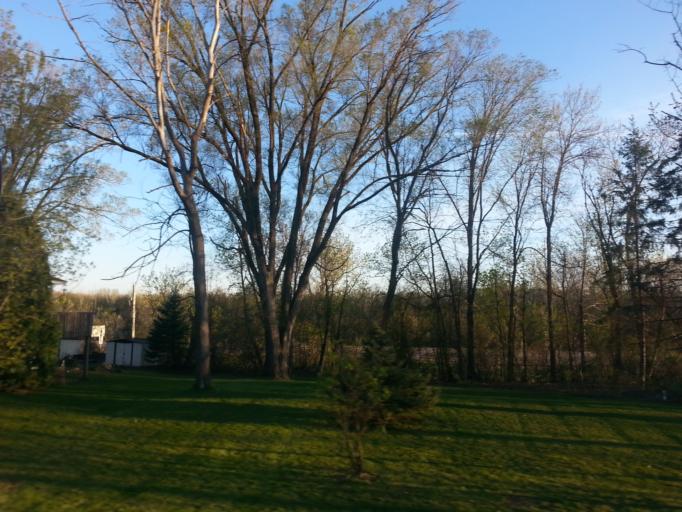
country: US
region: Wisconsin
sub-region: Pierce County
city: Prescott
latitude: 44.7510
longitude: -92.8168
